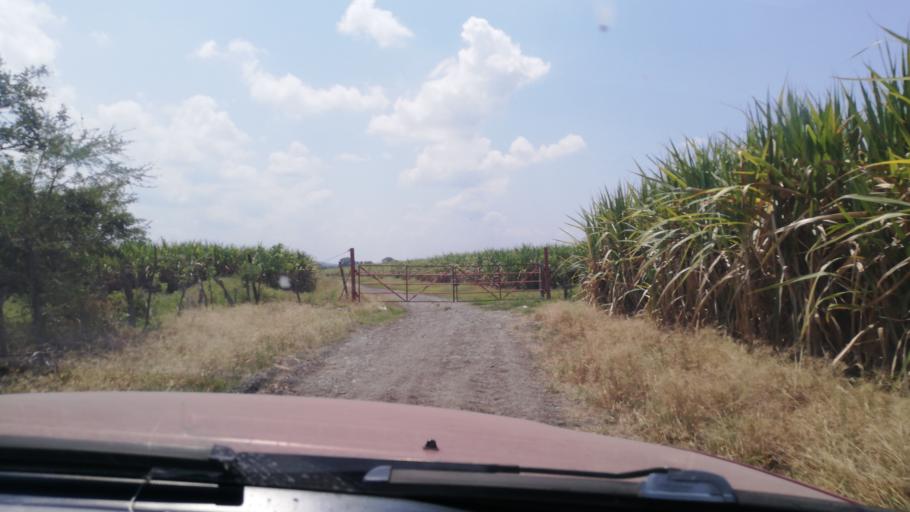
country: CO
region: Valle del Cauca
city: San Pedro
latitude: 3.9857
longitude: -76.2643
